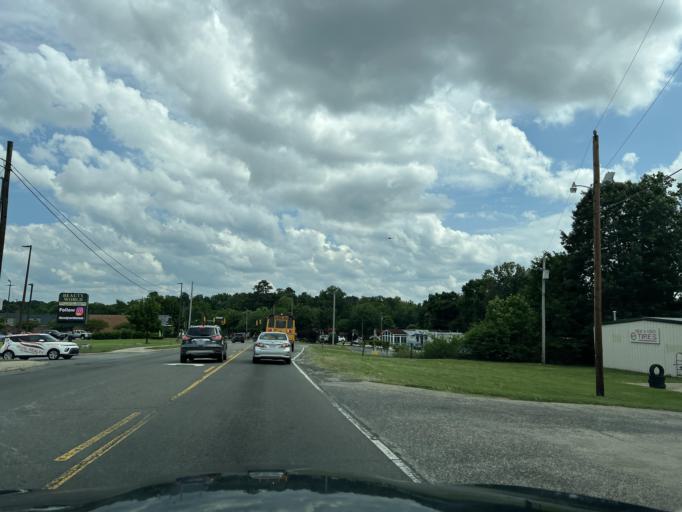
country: US
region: North Carolina
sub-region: Durham County
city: Durham
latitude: 36.0065
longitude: -78.8854
